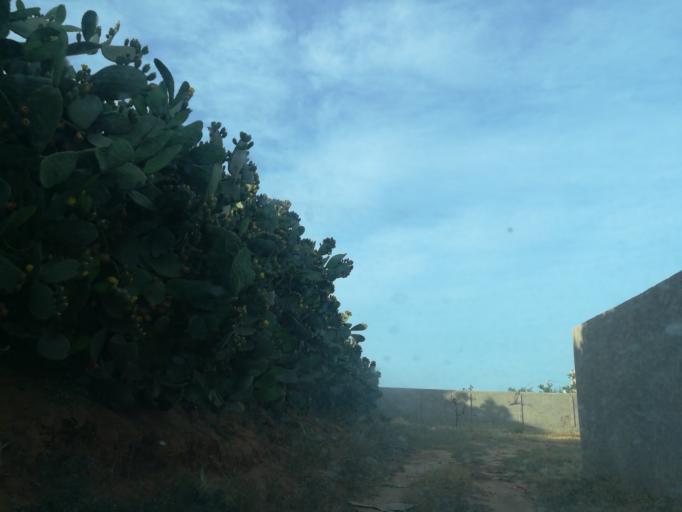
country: TN
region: Safaqis
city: Al Qarmadah
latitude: 34.8157
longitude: 10.7493
